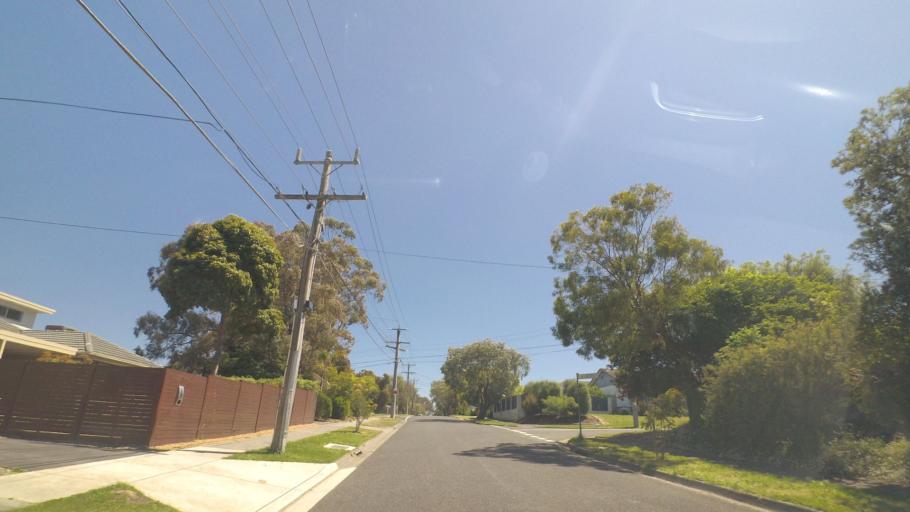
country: AU
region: Victoria
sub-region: Maroondah
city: Croydon Hills
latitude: -37.7858
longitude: 145.2723
